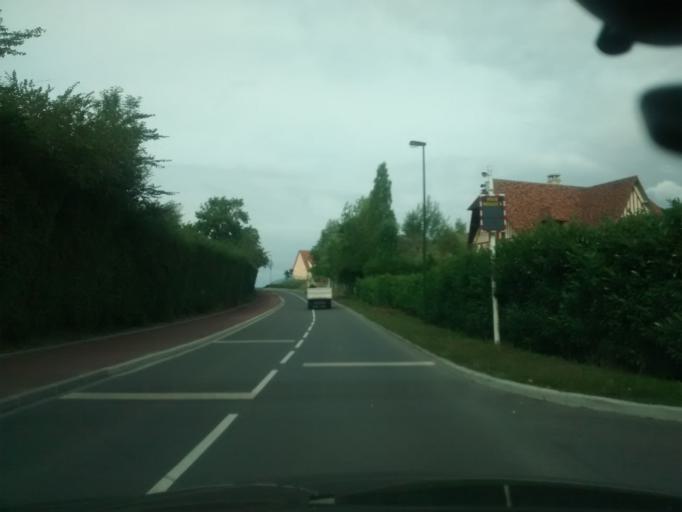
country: FR
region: Lower Normandy
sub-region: Departement du Calvados
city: Touques
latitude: 49.3307
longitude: 0.0875
